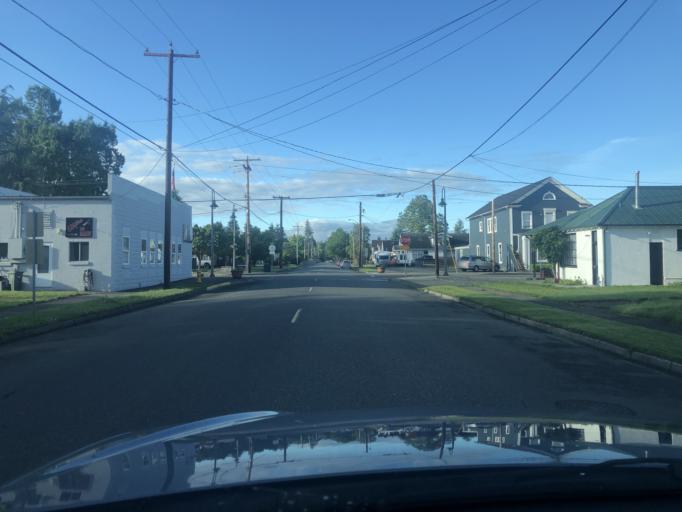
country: US
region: Washington
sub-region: Pierce County
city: Buckley
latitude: 47.1637
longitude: -122.0261
